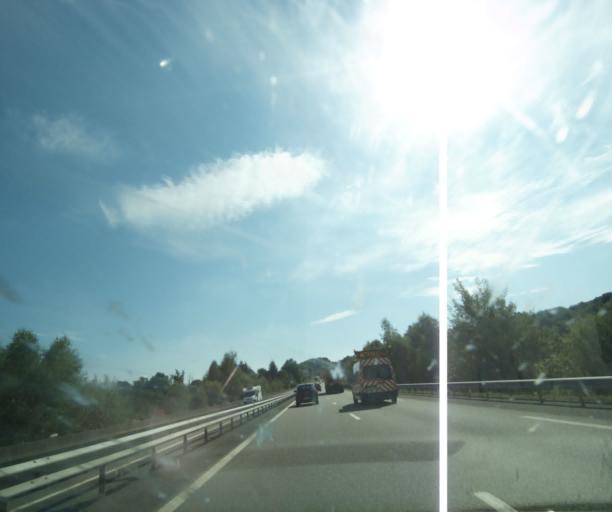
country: FR
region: Limousin
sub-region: Departement de la Correze
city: Sainte-Fereole
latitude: 45.2967
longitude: 1.5738
